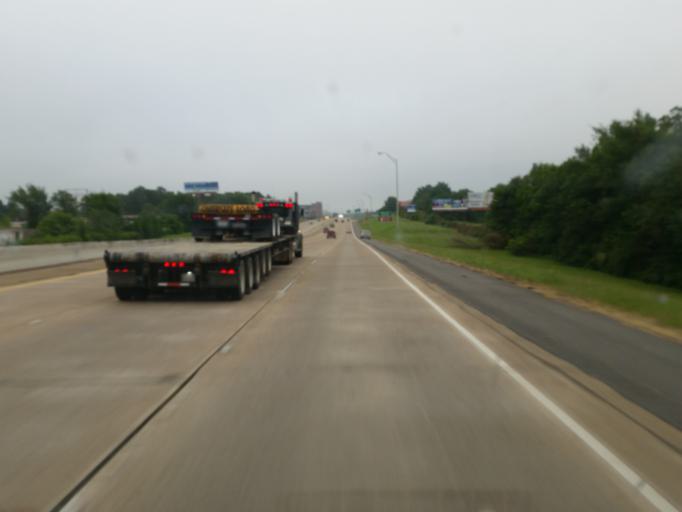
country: US
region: Louisiana
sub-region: Caddo Parish
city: Shreveport
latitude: 32.4695
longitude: -93.8055
